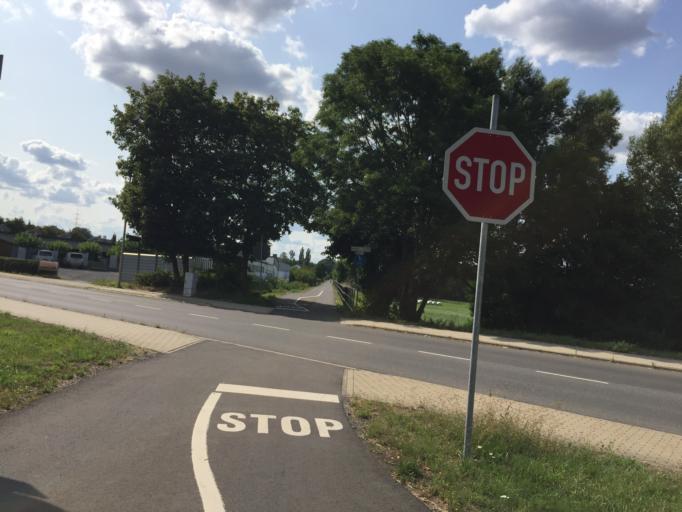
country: DE
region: Hesse
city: Schwalmstadt
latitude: 50.9051
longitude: 9.2224
